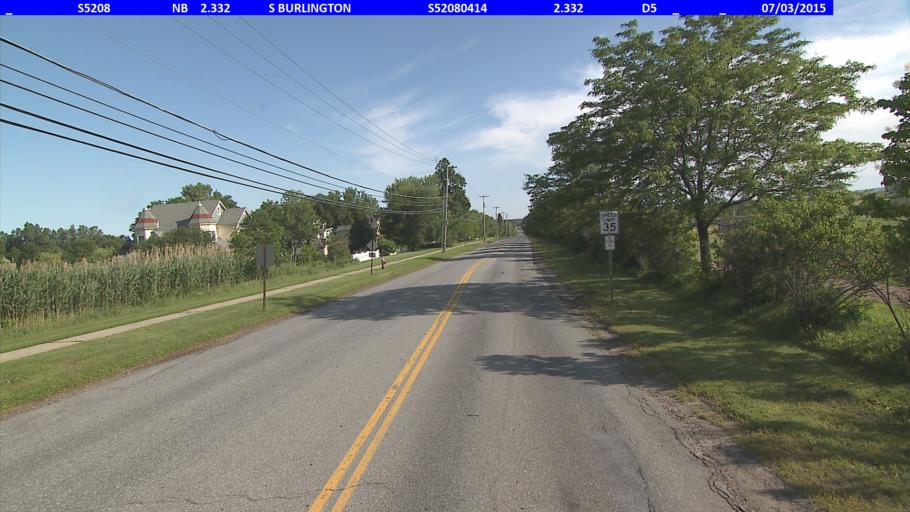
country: US
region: Vermont
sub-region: Chittenden County
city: South Burlington
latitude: 44.4440
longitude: -73.1772
